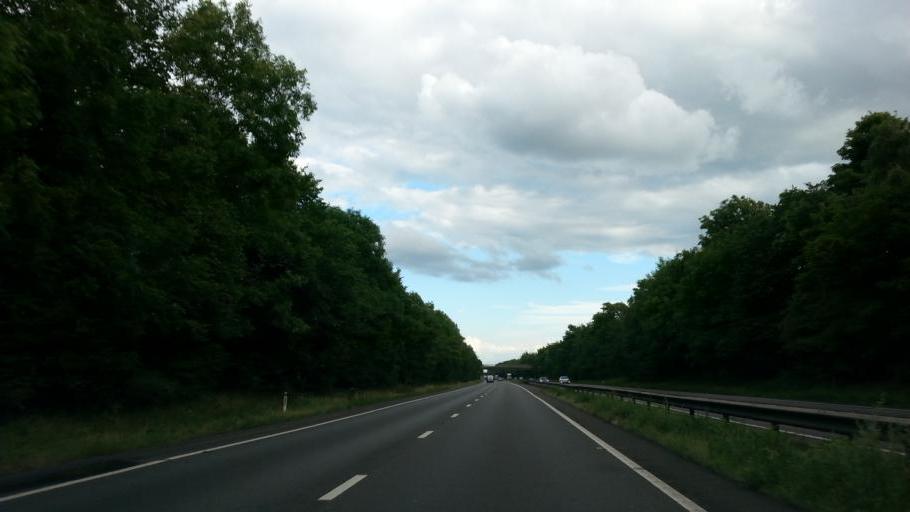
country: GB
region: England
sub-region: Nottinghamshire
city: Tuxford
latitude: 53.2103
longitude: -0.8717
